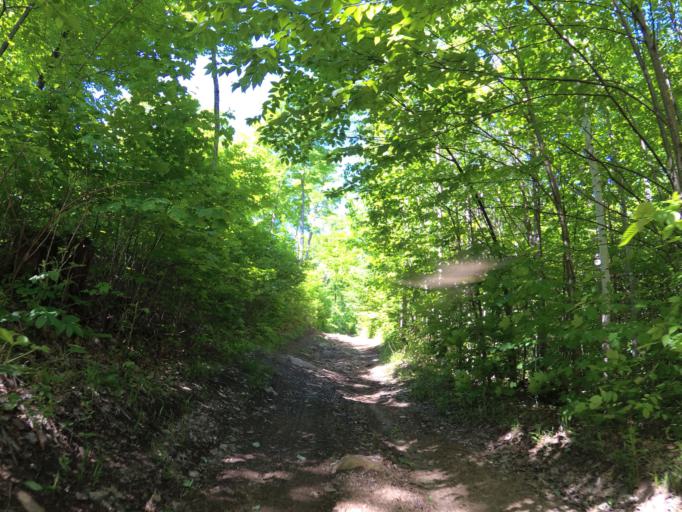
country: CA
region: Ontario
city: Renfrew
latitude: 45.0660
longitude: -77.0741
